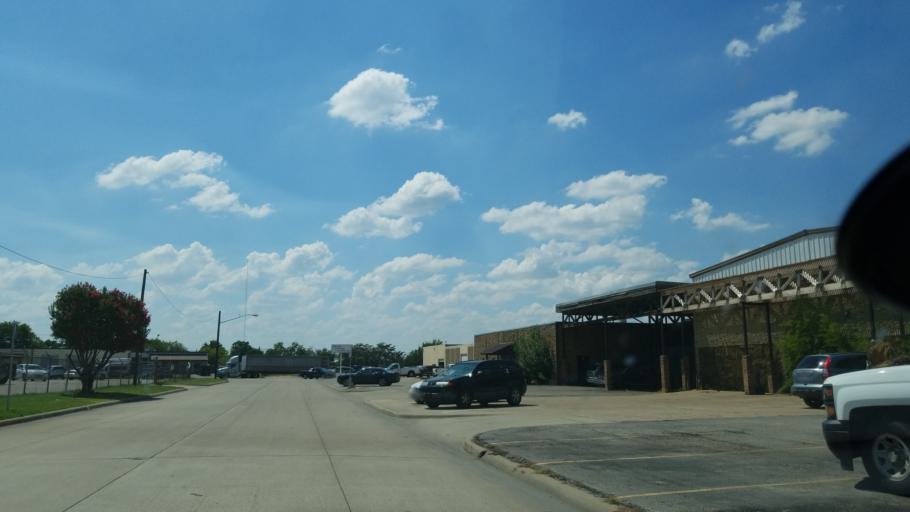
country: US
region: Texas
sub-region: Dallas County
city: Richardson
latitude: 32.9047
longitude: -96.6965
